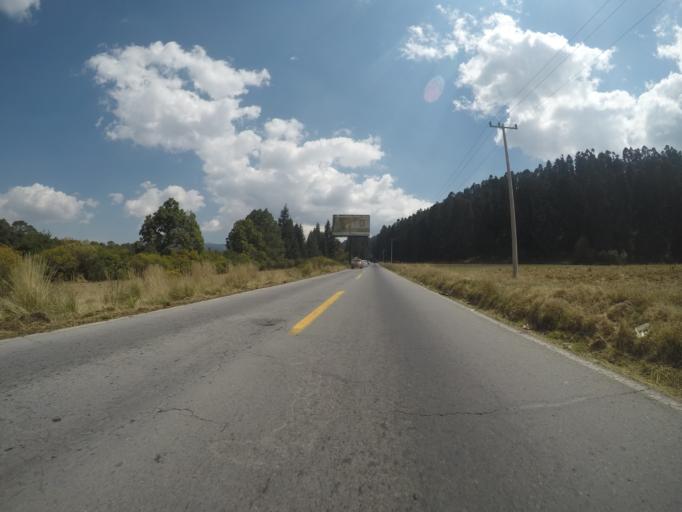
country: MX
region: Mexico
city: Cerro La Calera
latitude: 19.1970
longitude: -99.8089
